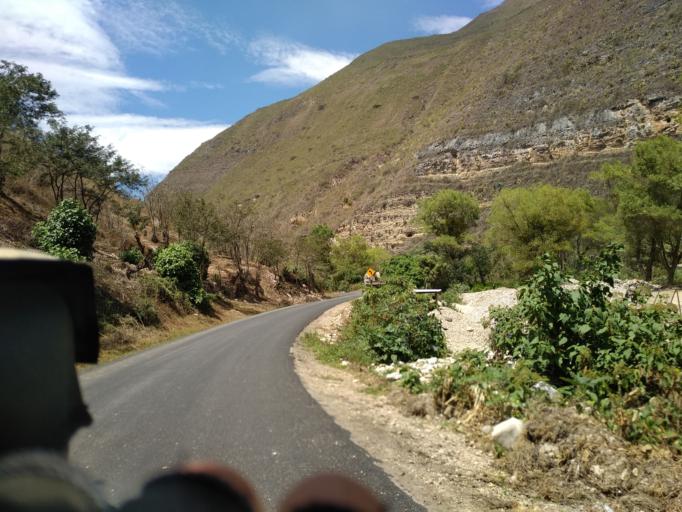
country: PE
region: Amazonas
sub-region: Provincia de Chachapoyas
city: Duraznopampa
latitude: -6.5788
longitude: -77.8244
